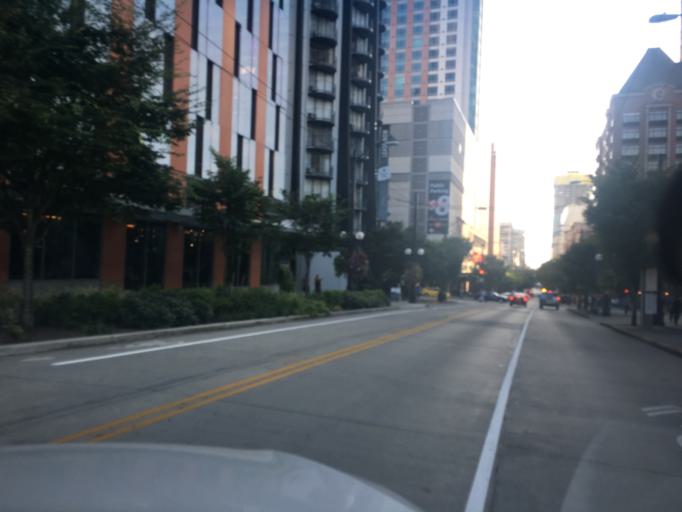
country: US
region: Washington
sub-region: King County
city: Seattle
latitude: 47.6135
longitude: -122.3322
